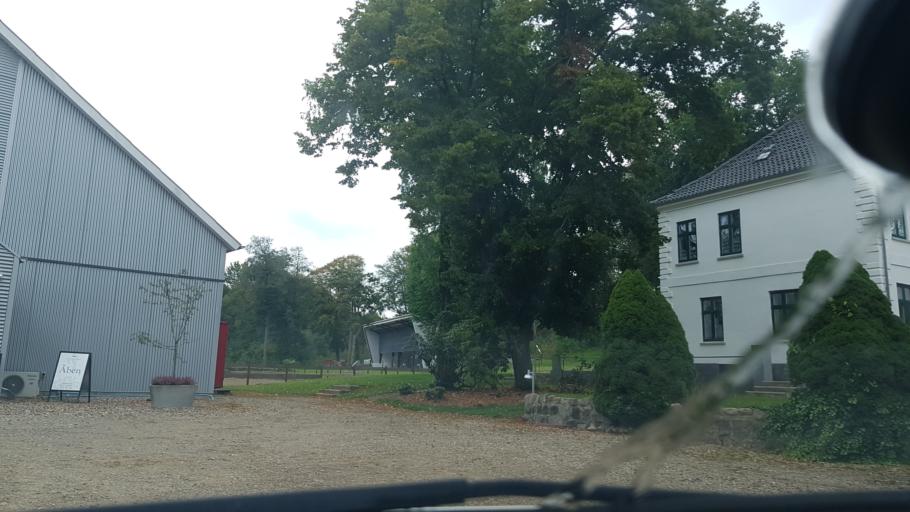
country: DK
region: South Denmark
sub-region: Kolding Kommune
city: Kolding
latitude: 55.5556
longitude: 9.4019
